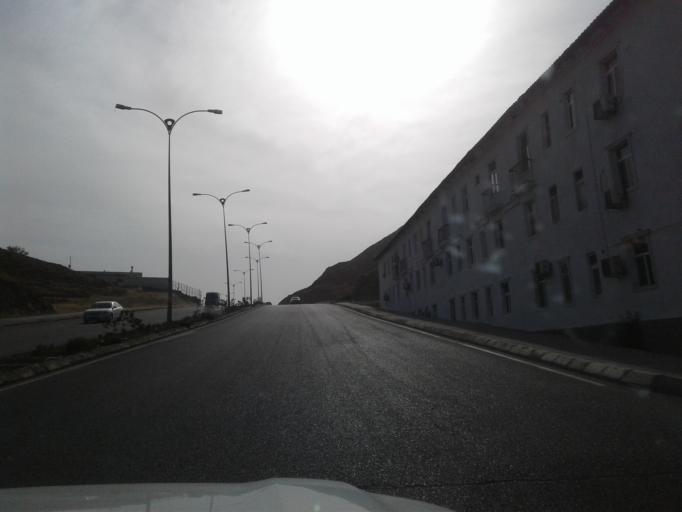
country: TM
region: Balkan
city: Turkmenbasy
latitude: 40.0024
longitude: 52.9816
